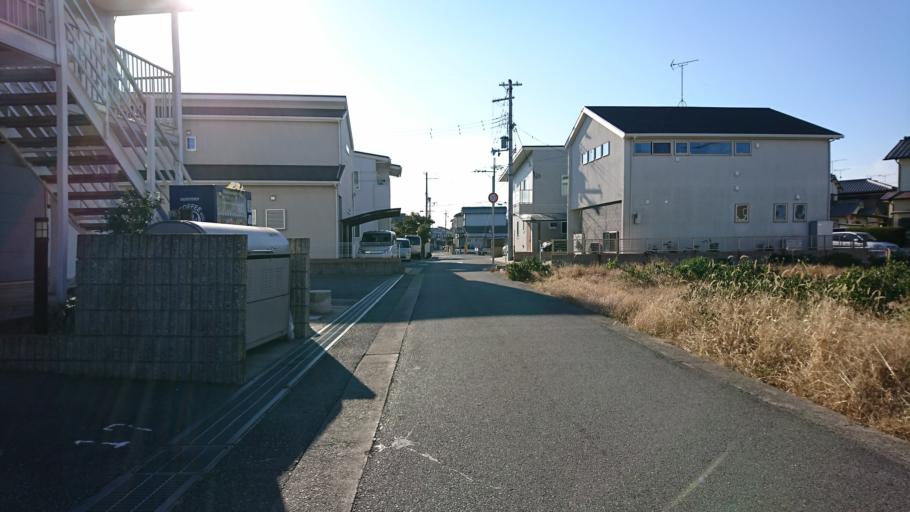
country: JP
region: Hyogo
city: Kakogawacho-honmachi
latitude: 34.7438
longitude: 134.8494
